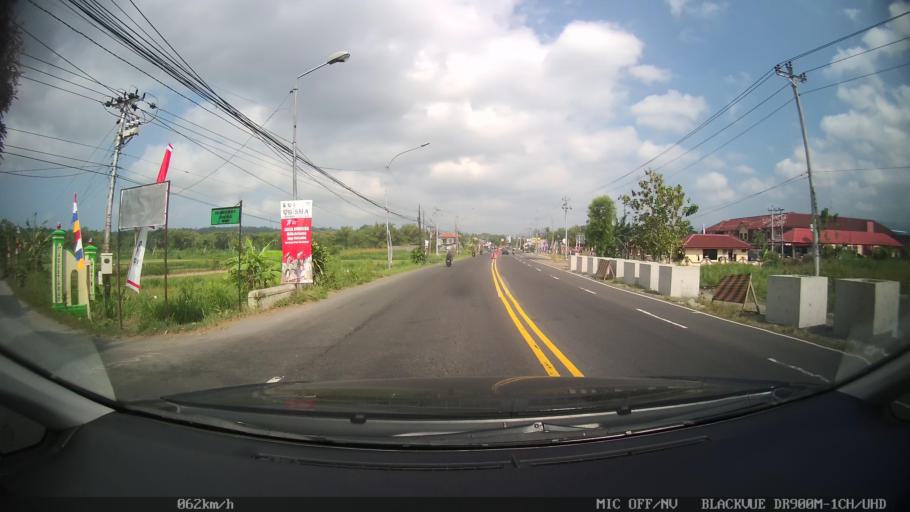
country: ID
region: Daerah Istimewa Yogyakarta
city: Srandakan
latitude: -7.8669
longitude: 110.1776
